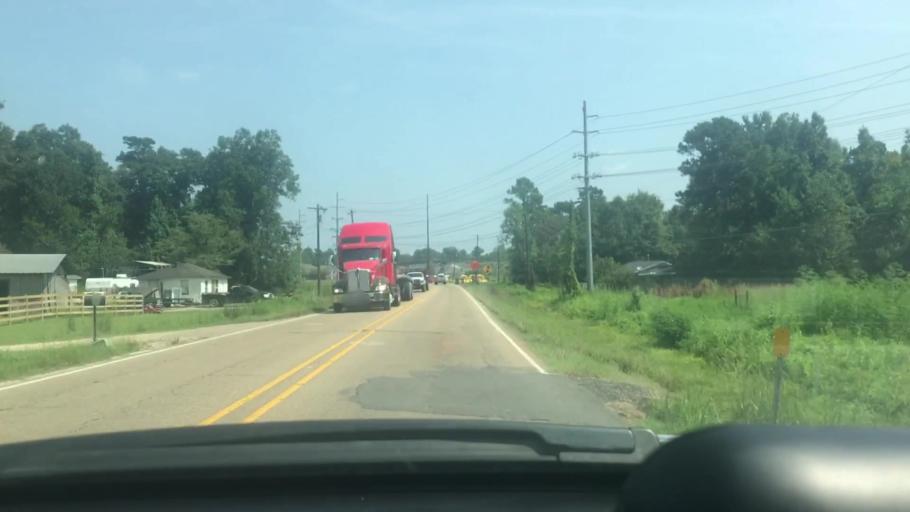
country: US
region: Louisiana
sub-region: Livingston Parish
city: Denham Springs
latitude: 30.4805
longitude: -90.9182
